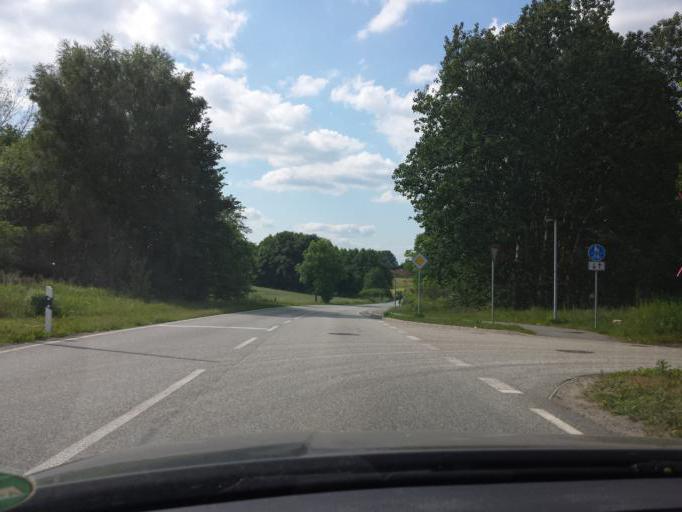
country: DE
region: Brandenburg
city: Neuruppin
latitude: 52.9415
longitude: 12.8563
